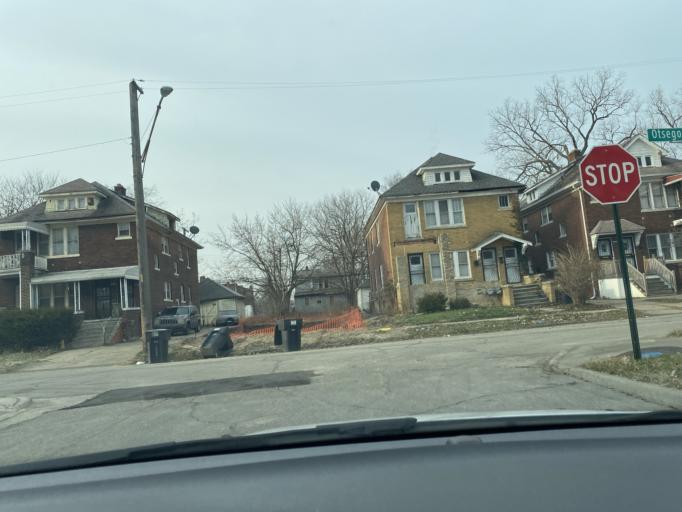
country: US
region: Michigan
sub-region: Wayne County
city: Highland Park
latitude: 42.3800
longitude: -83.1318
